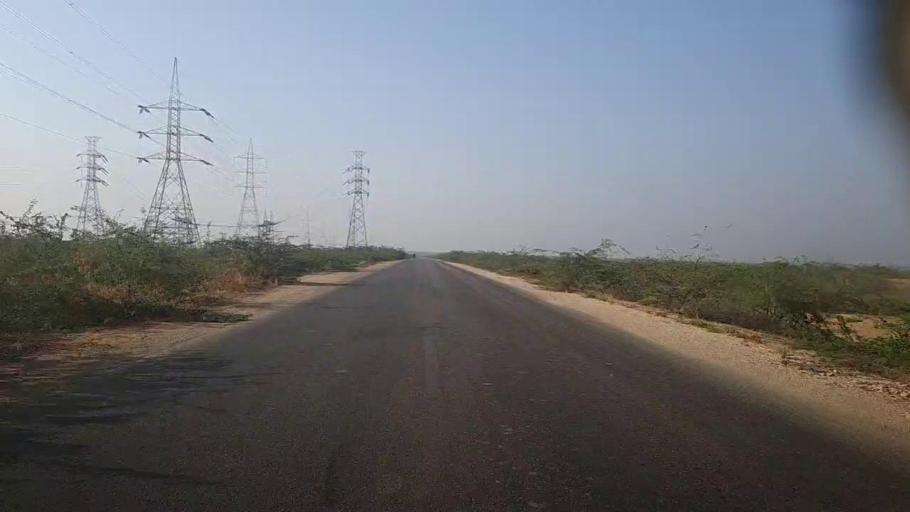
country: PK
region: Sindh
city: Gharo
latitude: 24.7623
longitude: 67.5446
